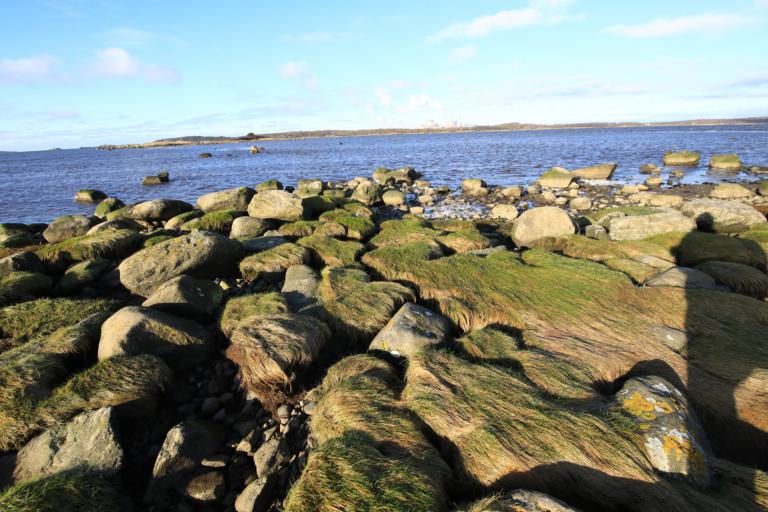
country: SE
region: Halland
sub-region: Kungsbacka Kommun
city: Frillesas
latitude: 57.2037
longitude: 12.1887
